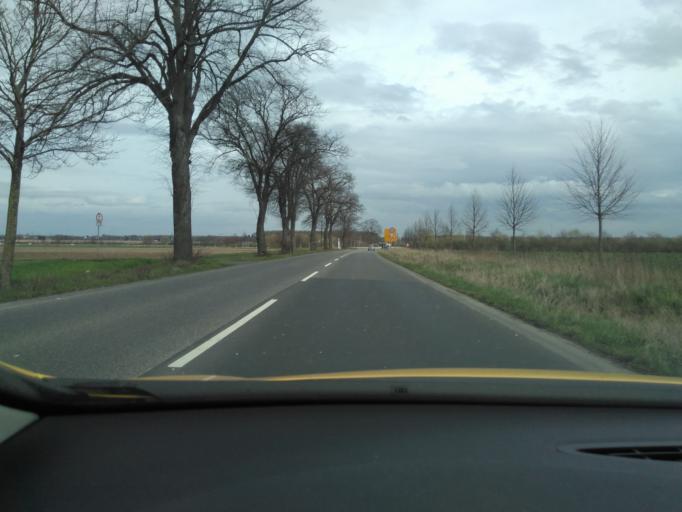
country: DE
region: North Rhine-Westphalia
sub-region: Regierungsbezirk Koln
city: Erftstadt
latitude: 50.8025
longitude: 6.7838
